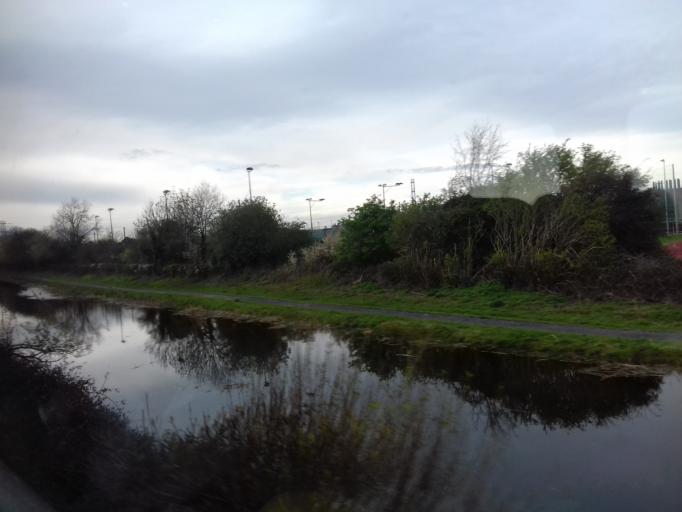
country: IE
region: Leinster
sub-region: Kildare
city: Leixlip
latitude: 53.3686
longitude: -6.5124
